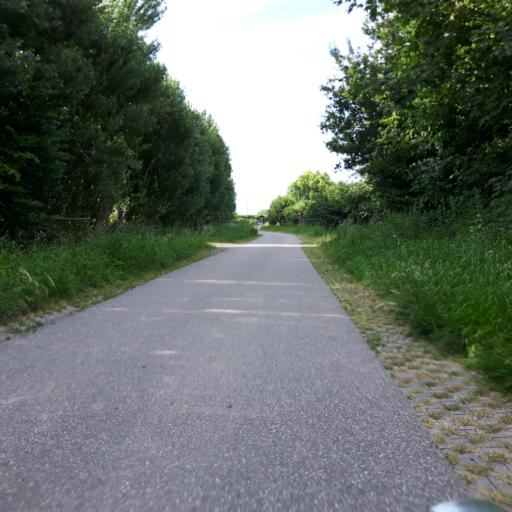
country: NL
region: Zeeland
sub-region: Gemeente Goes
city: Goes
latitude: 51.4850
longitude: 3.9403
